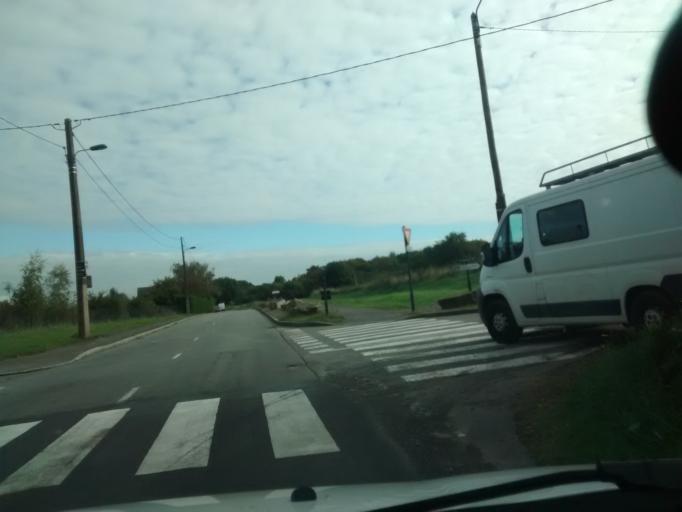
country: FR
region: Brittany
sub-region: Departement d'Ille-et-Vilaine
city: Saint-Jacques-de-la-Lande
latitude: 48.0980
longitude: -1.7273
